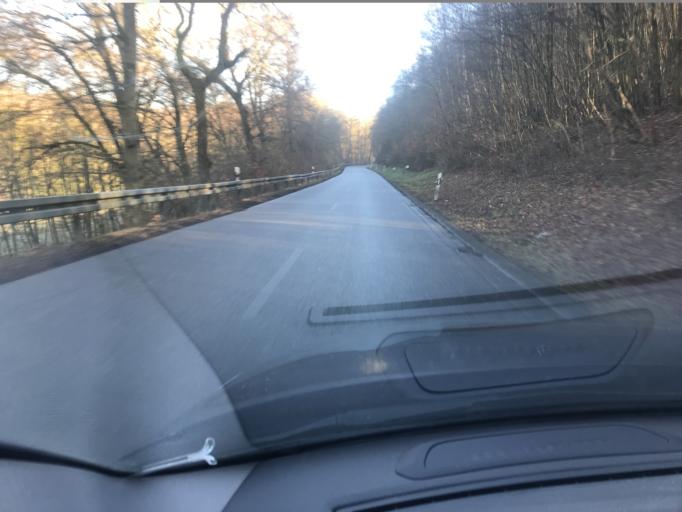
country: DE
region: Rheinland-Pfalz
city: Niedererbach
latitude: 50.4212
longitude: 7.9925
